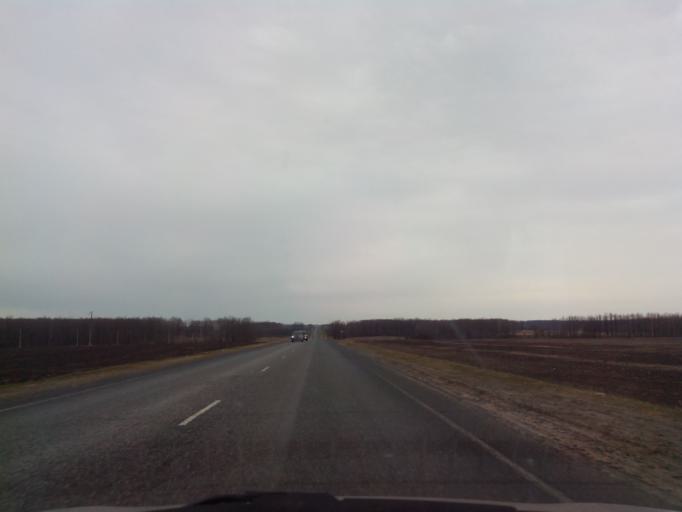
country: RU
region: Tambov
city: Zavoronezhskoye
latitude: 52.9925
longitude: 40.5536
